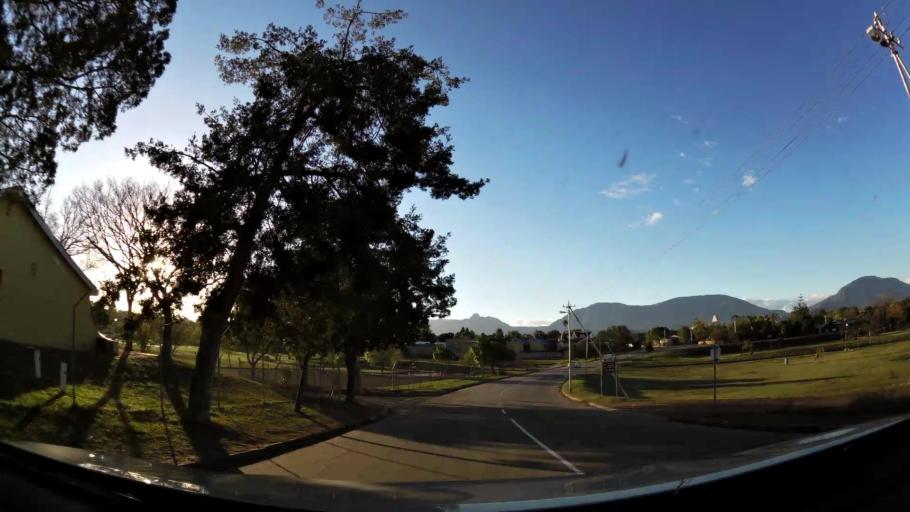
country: ZA
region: Western Cape
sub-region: Eden District Municipality
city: Riversdale
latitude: -34.0882
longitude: 21.2480
